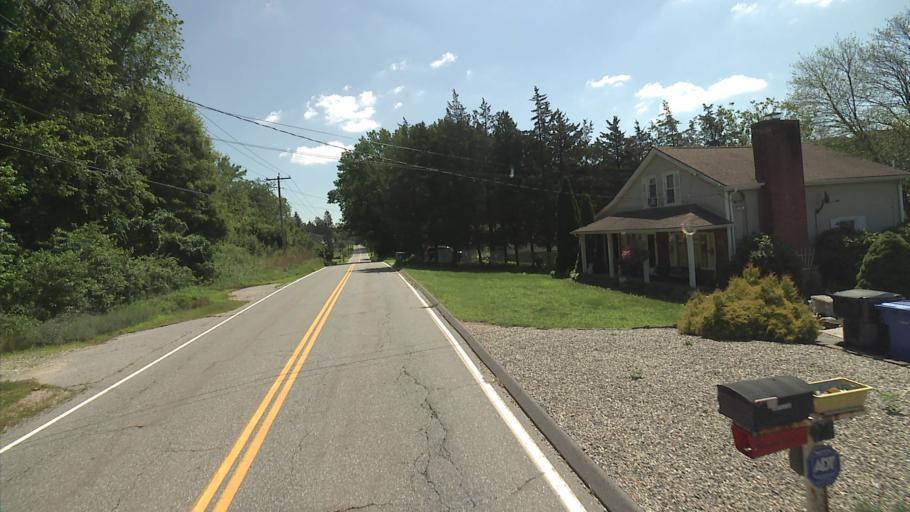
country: US
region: Connecticut
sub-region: Windham County
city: Plainfield Village
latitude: 41.6864
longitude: -71.9407
